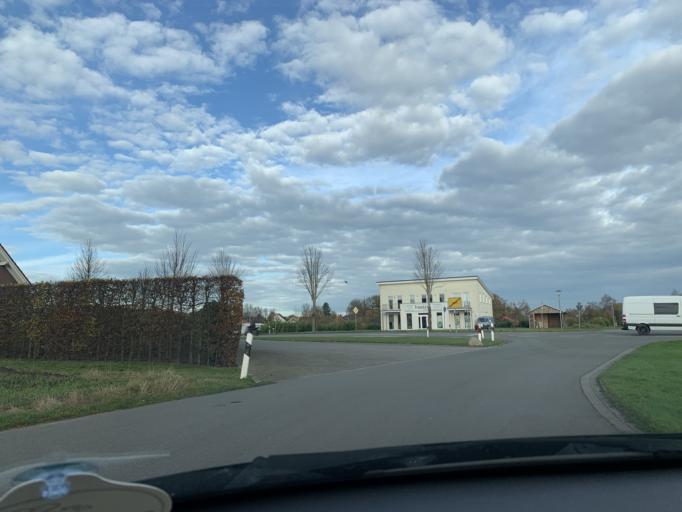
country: DE
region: Lower Saxony
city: Apen
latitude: 53.2146
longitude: 7.8058
